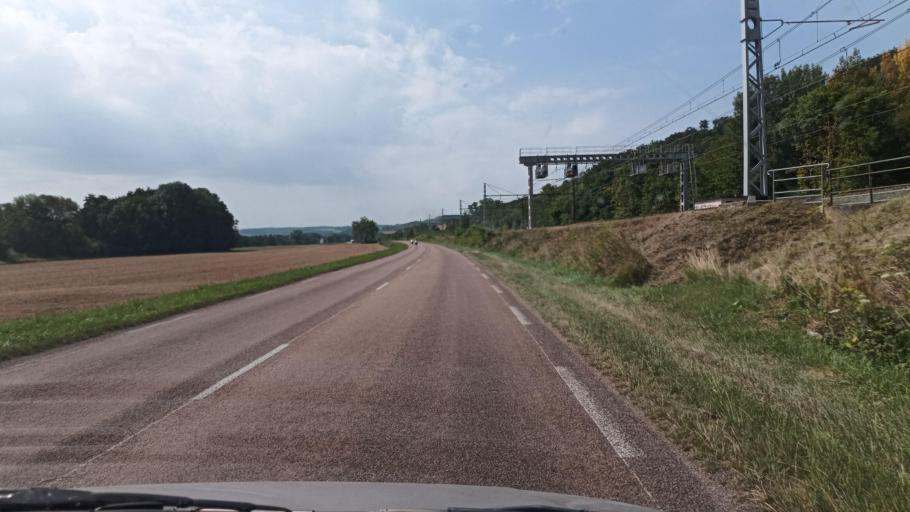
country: FR
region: Bourgogne
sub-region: Departement de l'Yonne
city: Veron
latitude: 48.1254
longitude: 3.2795
